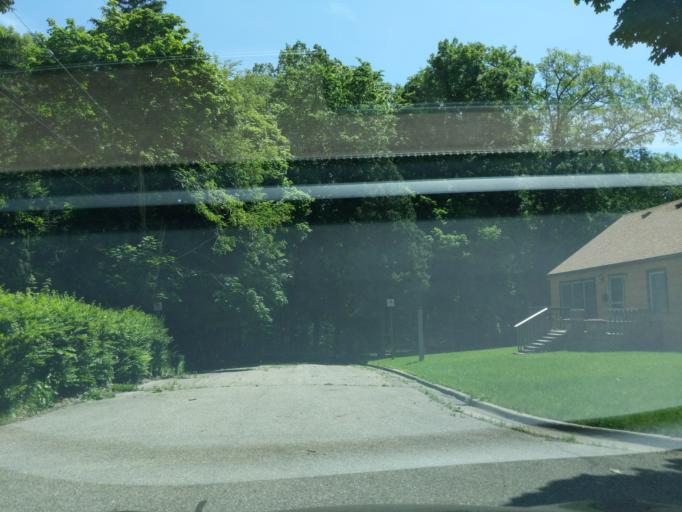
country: US
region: Michigan
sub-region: Ingham County
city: Lansing
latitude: 42.7517
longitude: -84.5310
